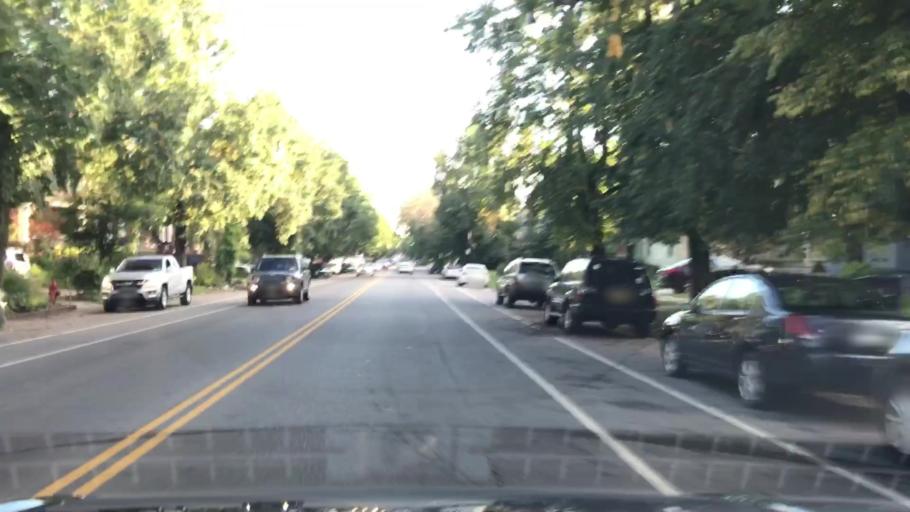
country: US
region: New York
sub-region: Erie County
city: Buffalo
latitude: 42.9105
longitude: -78.8820
